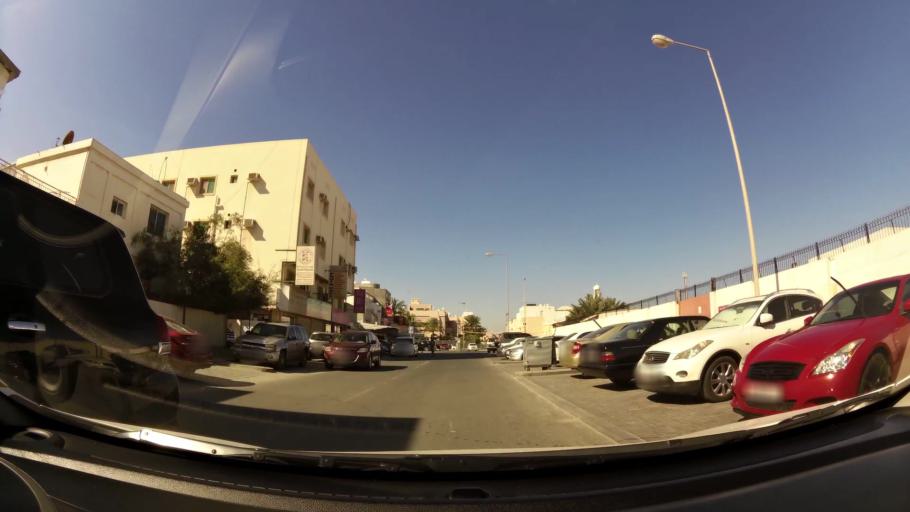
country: BH
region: Muharraq
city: Al Hadd
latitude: 26.2409
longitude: 50.6554
